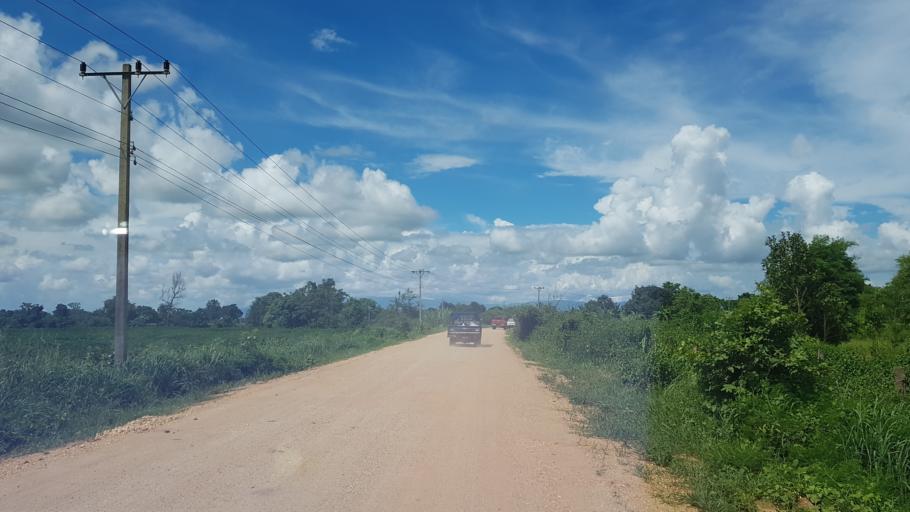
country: LA
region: Vientiane
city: Vientiane
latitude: 18.2334
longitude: 102.5291
